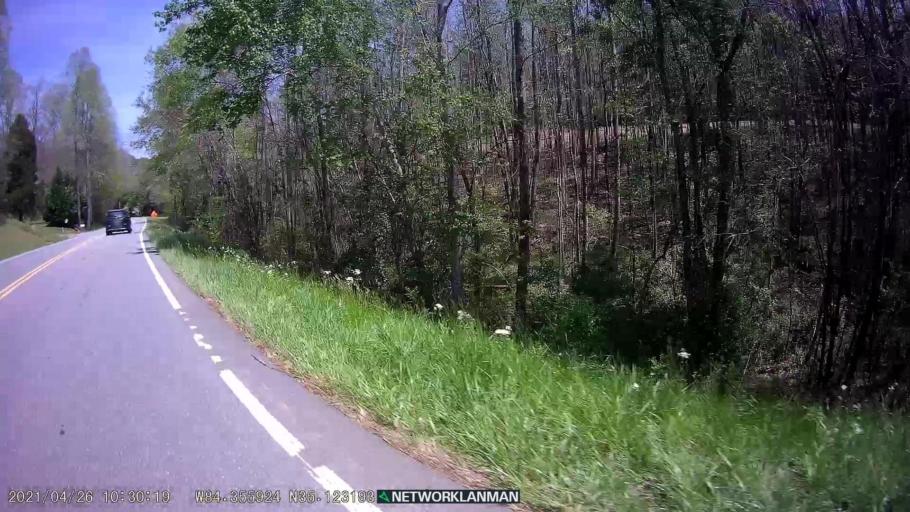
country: US
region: Georgia
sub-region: Fannin County
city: McCaysville
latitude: 35.1234
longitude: -84.3559
